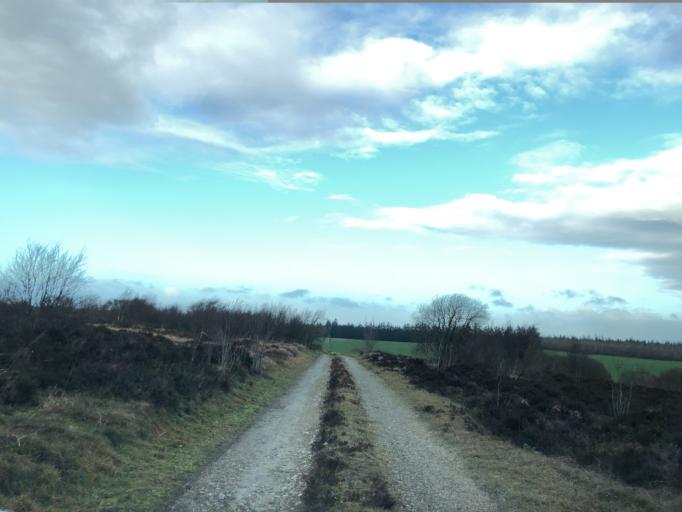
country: DK
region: Central Jutland
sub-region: Ringkobing-Skjern Kommune
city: Videbaek
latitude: 56.1861
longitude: 8.6605
